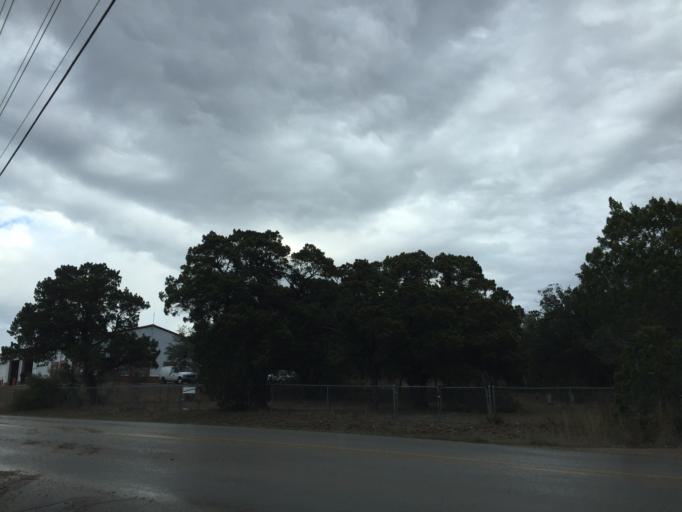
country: US
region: Texas
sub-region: Travis County
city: Jonestown
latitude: 30.5725
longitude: -97.9492
